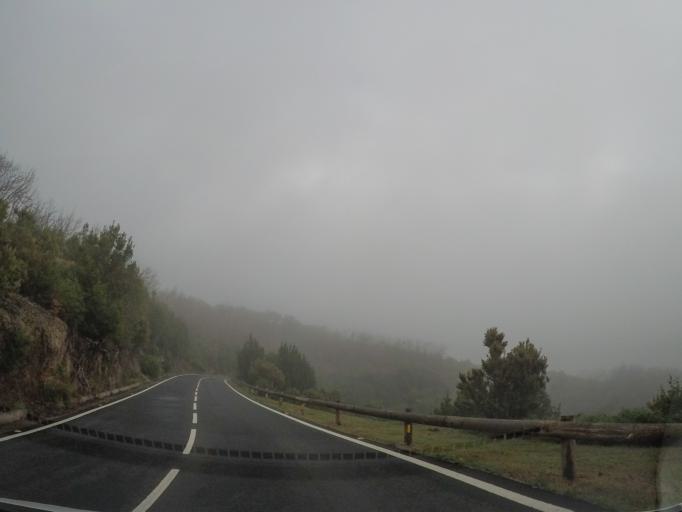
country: ES
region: Canary Islands
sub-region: Provincia de Santa Cruz de Tenerife
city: Vallehermosa
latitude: 28.1328
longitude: -17.2796
